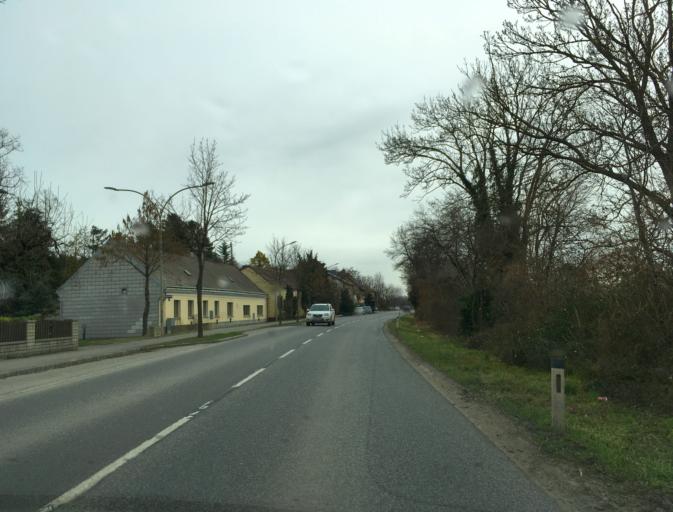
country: AT
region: Lower Austria
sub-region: Politischer Bezirk Ganserndorf
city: Deutsch-Wagram
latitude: 48.2941
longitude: 16.5596
